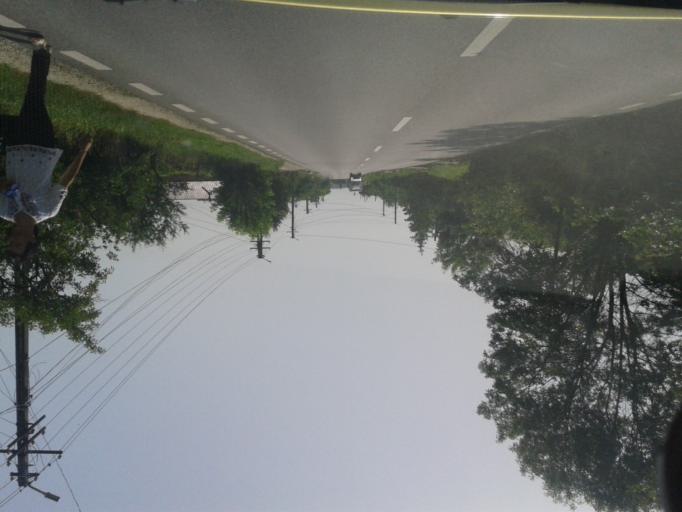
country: RO
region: Arges
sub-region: Comuna Babana
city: Babana
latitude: 44.9056
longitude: 24.7294
